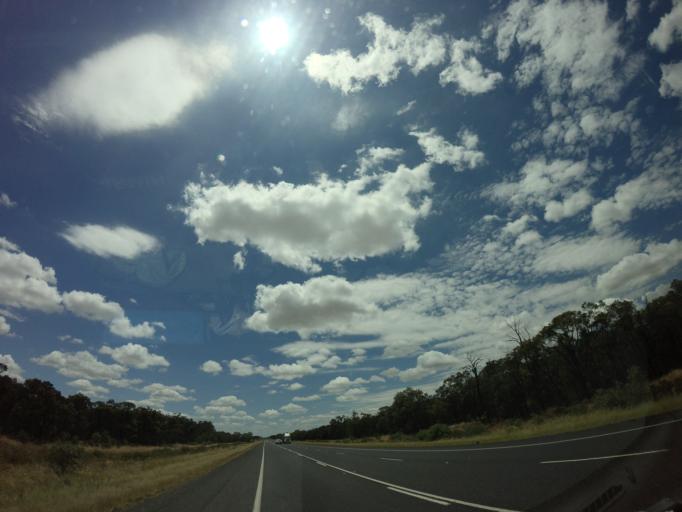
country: AU
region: New South Wales
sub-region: Moree Plains
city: Boggabilla
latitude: -28.8712
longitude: 150.1784
